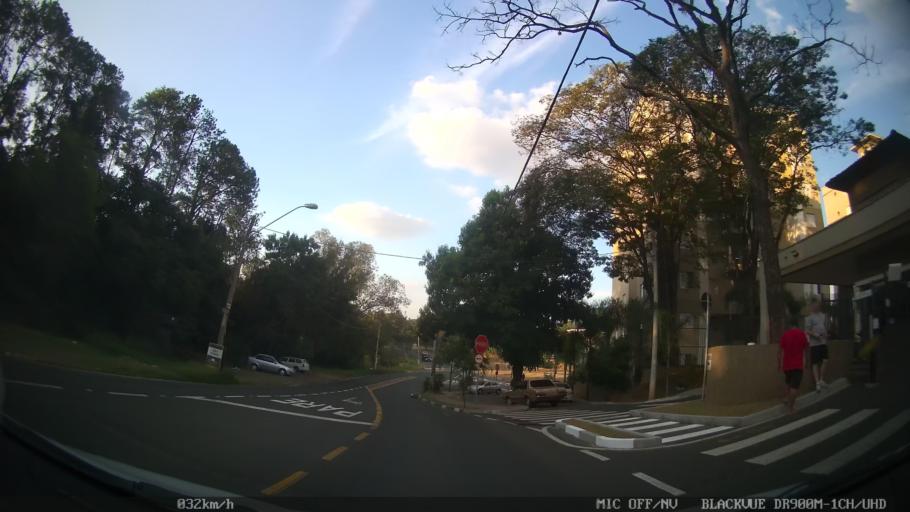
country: BR
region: Sao Paulo
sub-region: Hortolandia
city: Hortolandia
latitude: -22.8925
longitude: -47.1515
